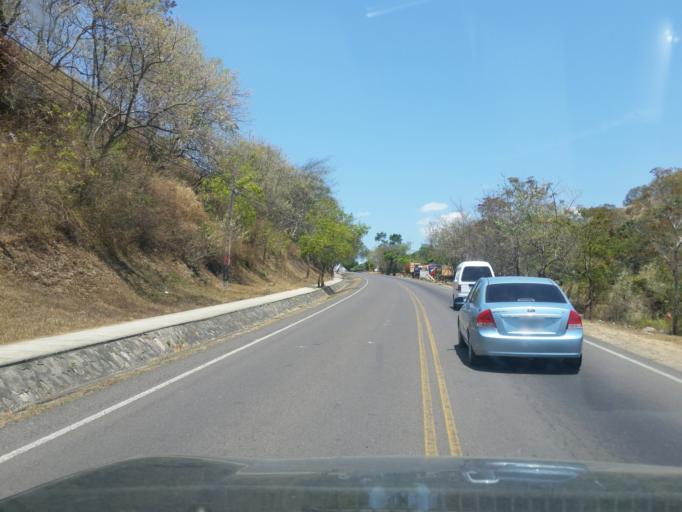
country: NI
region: Esteli
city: Esteli
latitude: 13.0092
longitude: -86.3091
